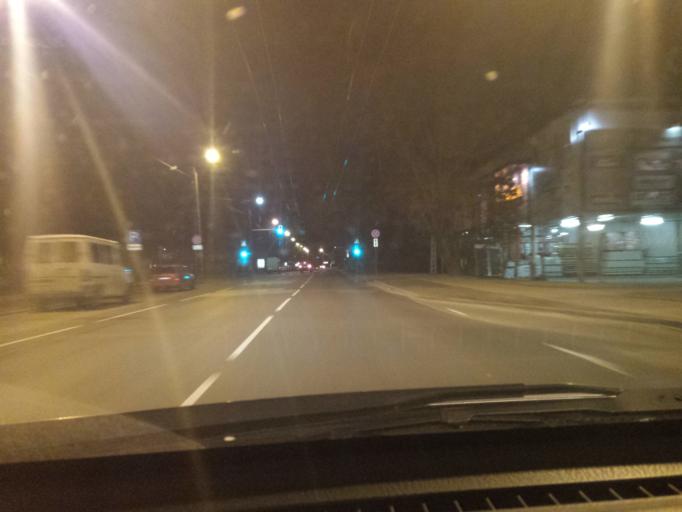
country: LV
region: Riga
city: Riga
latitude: 56.9620
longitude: 24.1761
